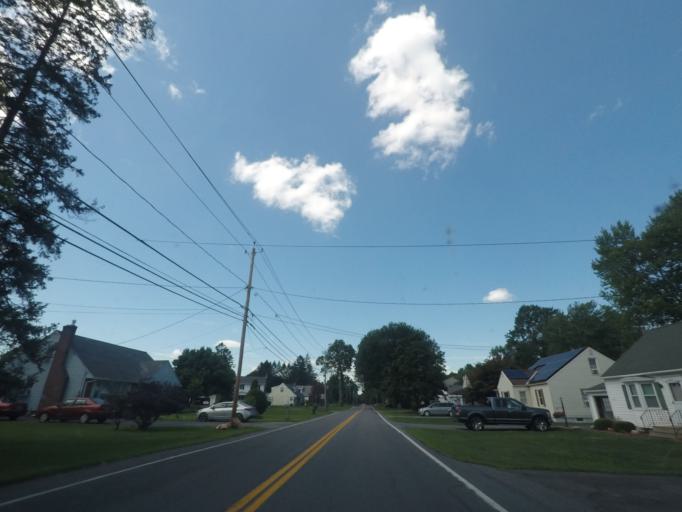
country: US
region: New York
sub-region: Schenectady County
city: Rotterdam
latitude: 42.7593
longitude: -73.9608
